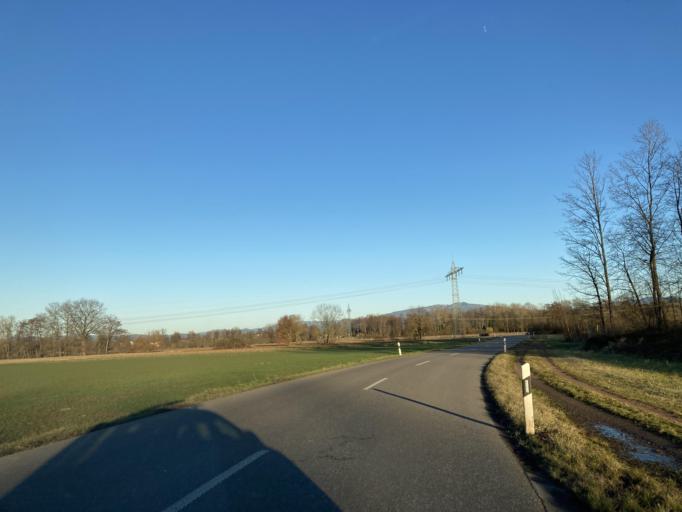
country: DE
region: Baden-Wuerttemberg
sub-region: Freiburg Region
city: Umkirch
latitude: 48.0543
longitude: 7.7625
